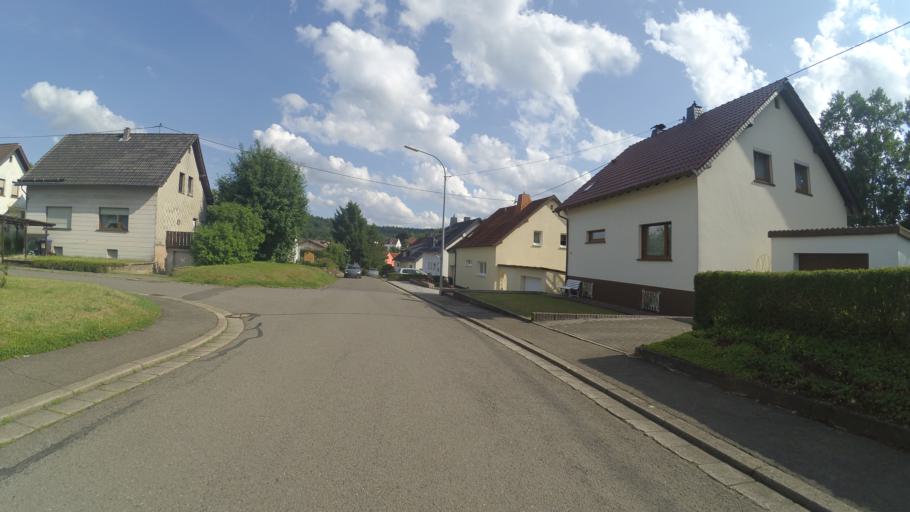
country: DE
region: Saarland
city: Nohfelden
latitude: 49.5813
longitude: 7.1466
